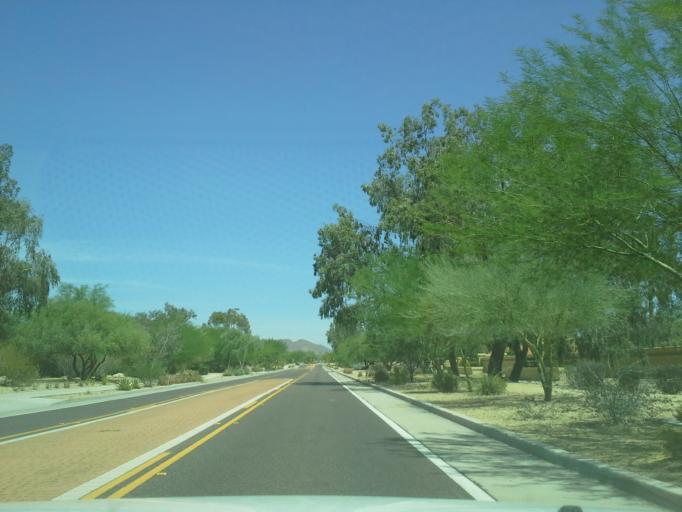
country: US
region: Arizona
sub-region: Maricopa County
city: Scottsdale
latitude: 33.5970
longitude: -111.8608
